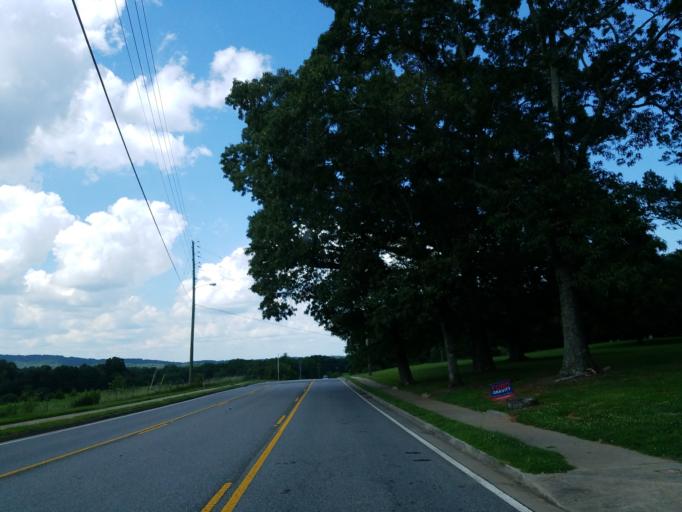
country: US
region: Georgia
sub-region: Forsyth County
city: Cumming
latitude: 34.2153
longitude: -84.1273
